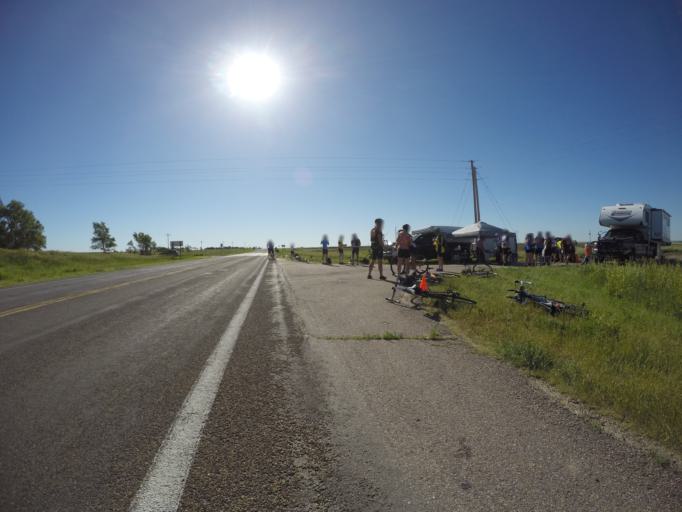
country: US
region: Kansas
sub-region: Norton County
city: Norton
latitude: 39.8276
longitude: -100.0054
